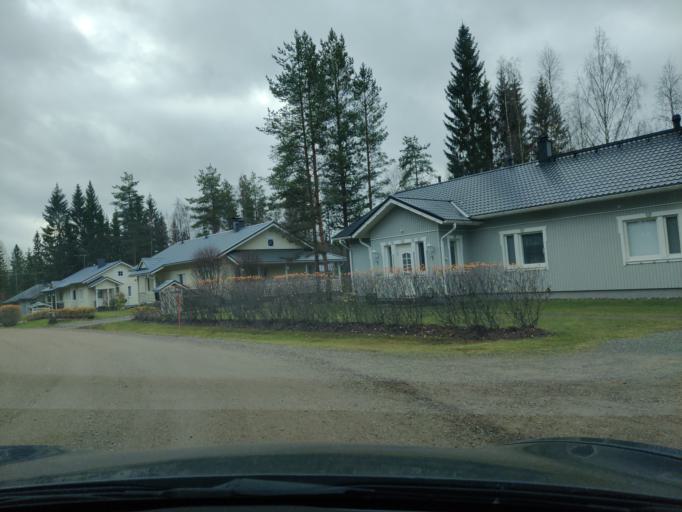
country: FI
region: Northern Savo
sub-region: Ylae-Savo
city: Kiuruvesi
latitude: 63.6417
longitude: 26.6376
